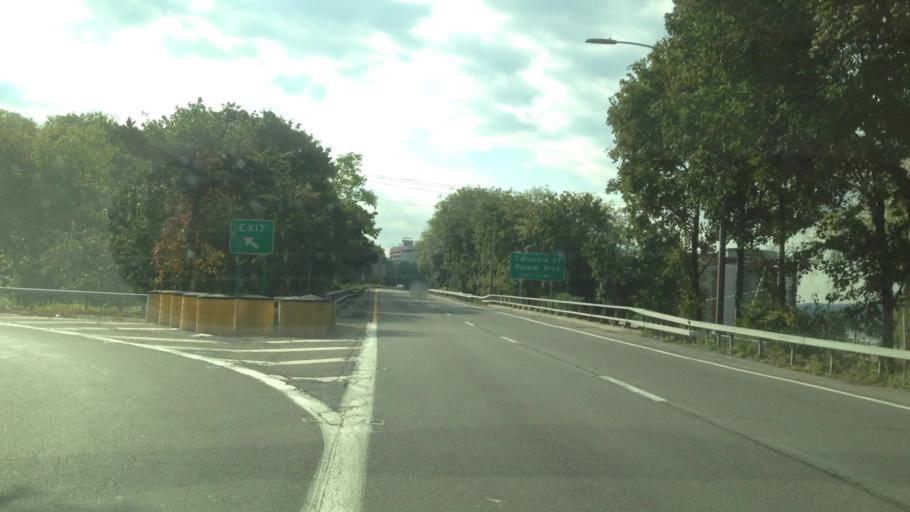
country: US
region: New York
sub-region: Dutchess County
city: Poughkeepsie
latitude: 41.7008
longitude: -73.9368
